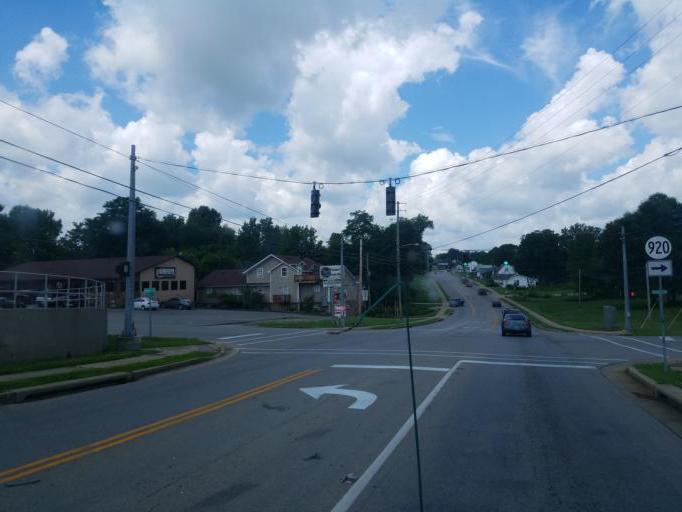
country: US
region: Kentucky
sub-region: Grayson County
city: Leitchfield
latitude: 37.4845
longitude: -86.2873
